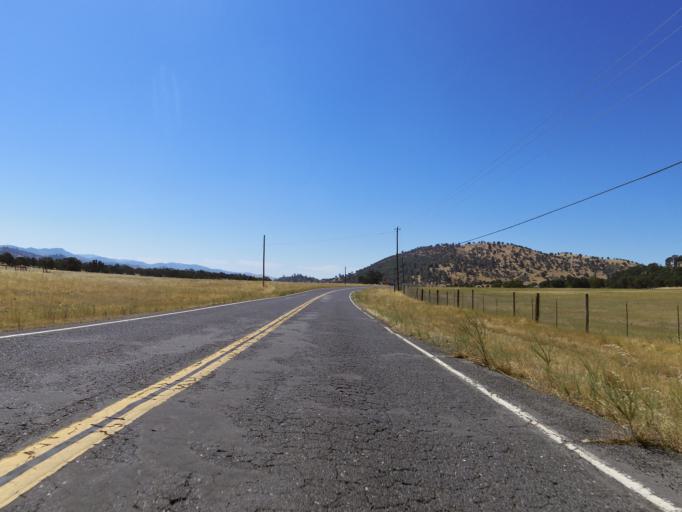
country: US
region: California
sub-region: Tuolumne County
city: Tuolumne City
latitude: 37.6415
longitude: -120.3084
